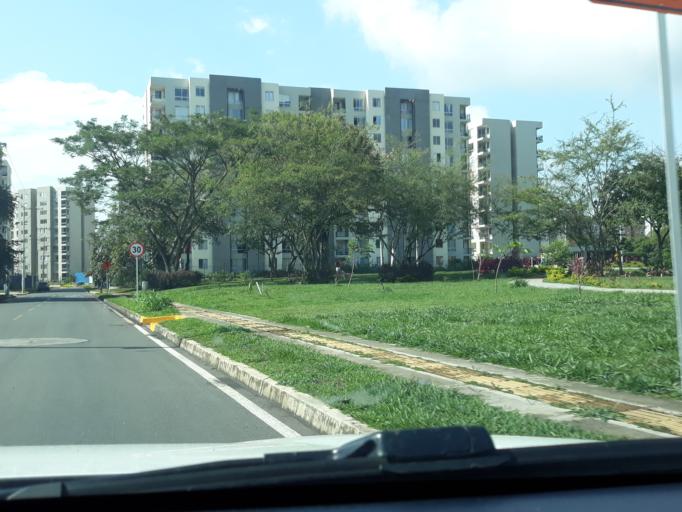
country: CO
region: Valle del Cauca
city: Cali
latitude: 3.3576
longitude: -76.5149
